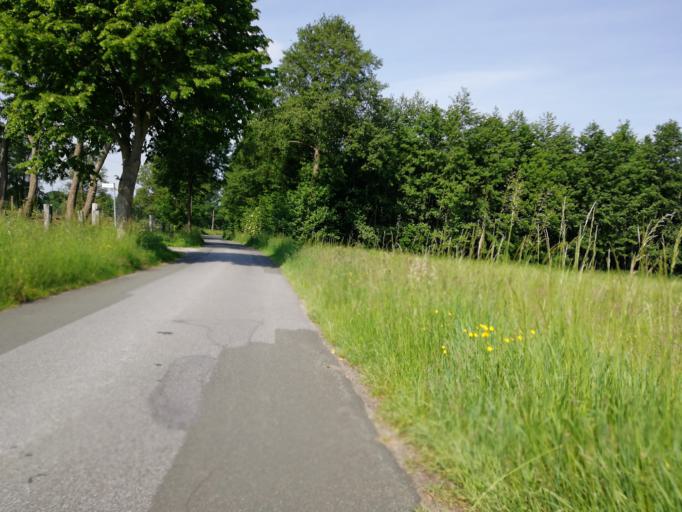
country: DE
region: North Rhine-Westphalia
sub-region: Regierungsbezirk Detmold
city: Verl
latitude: 51.9037
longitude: 8.5114
